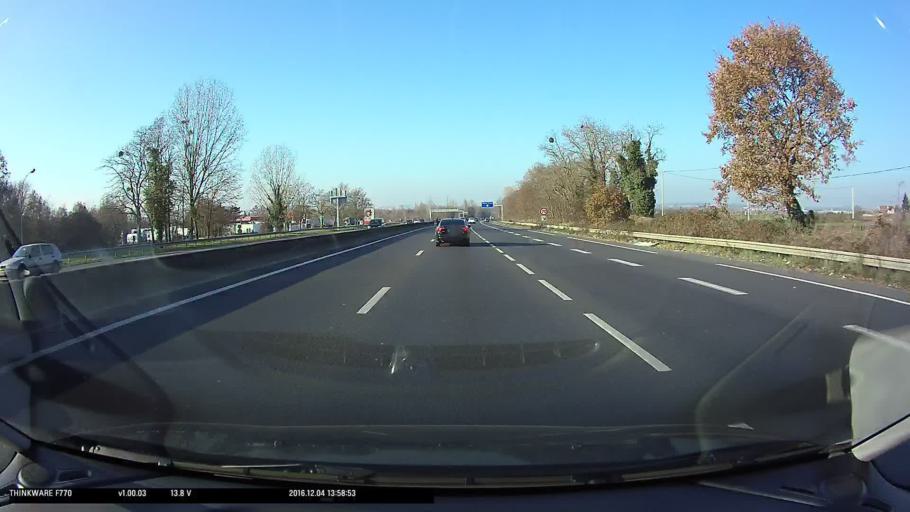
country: FR
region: Ile-de-France
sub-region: Departement du Val-d'Oise
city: Pierrelaye
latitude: 49.0120
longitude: 2.1514
